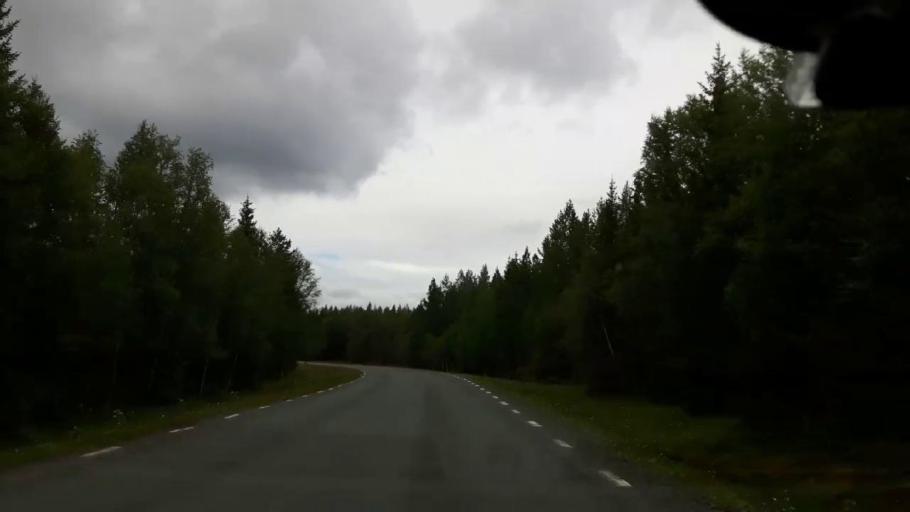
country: SE
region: Jaemtland
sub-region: Krokoms Kommun
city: Valla
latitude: 63.6167
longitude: 13.8127
